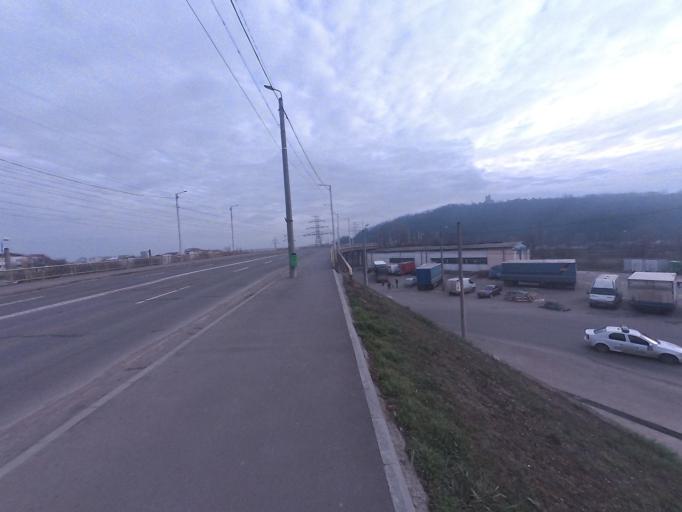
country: RO
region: Iasi
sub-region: Comuna Ciurea
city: Lunca Cetatuii
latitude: 47.1339
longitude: 27.5767
